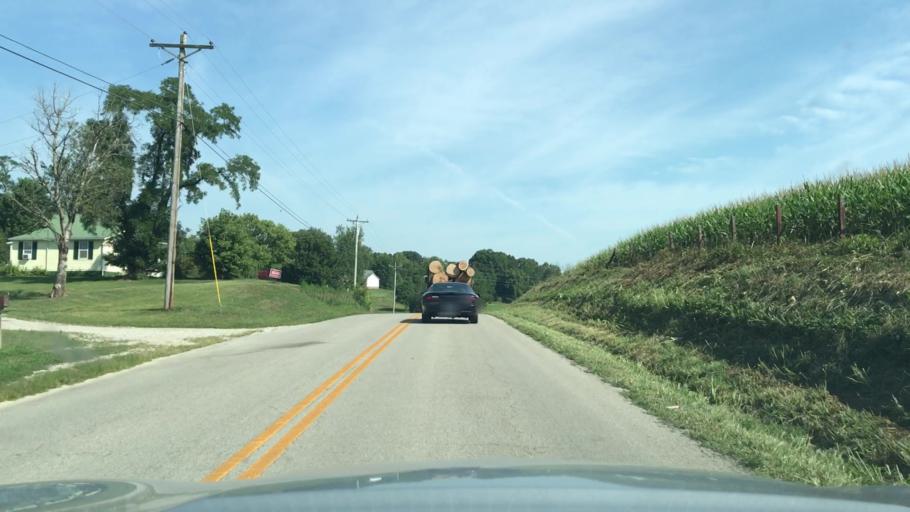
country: US
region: Kentucky
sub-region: Clinton County
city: Albany
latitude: 36.7561
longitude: -84.9971
